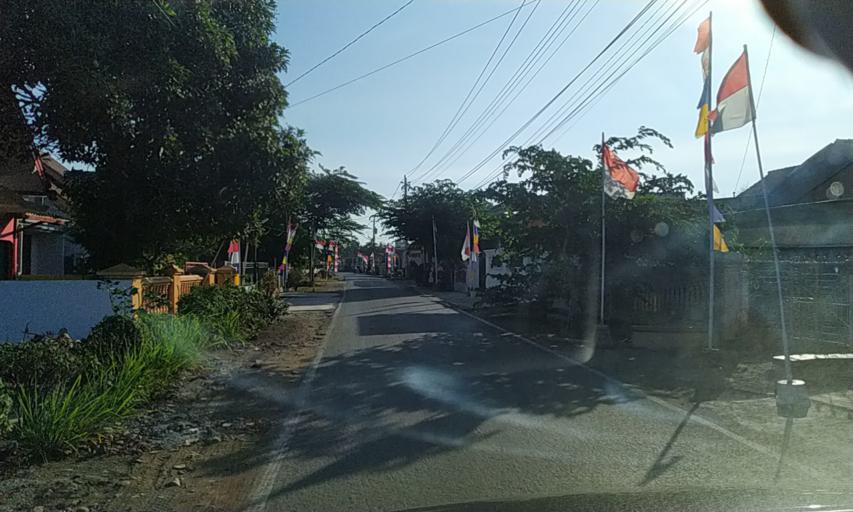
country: ID
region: Central Java
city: Rejanegara
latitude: -7.6775
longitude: 109.0504
